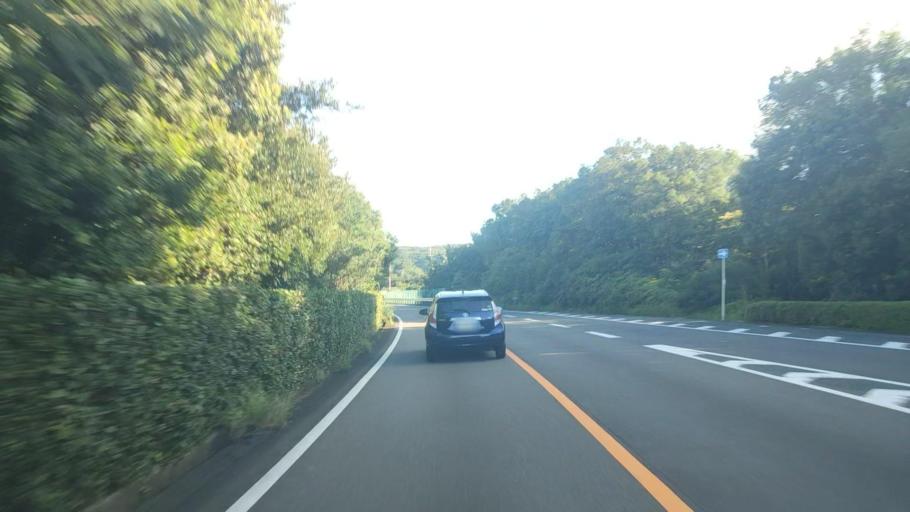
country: JP
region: Mie
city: Toba
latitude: 34.3559
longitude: 136.8453
